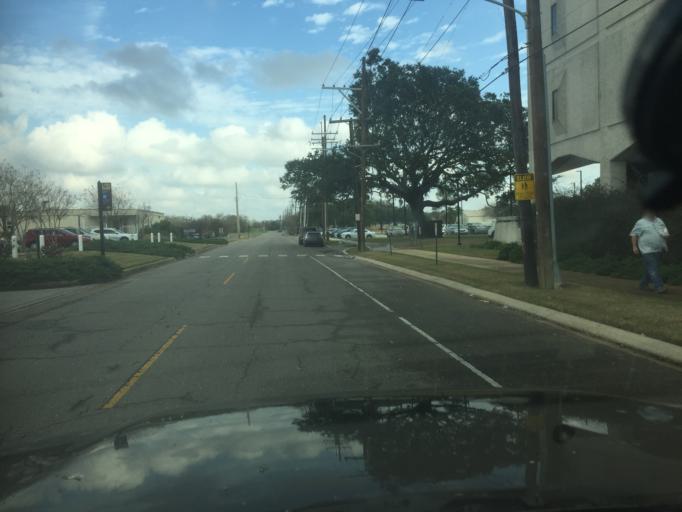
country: US
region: Louisiana
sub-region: Orleans Parish
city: New Orleans
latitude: 29.9918
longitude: -90.0840
